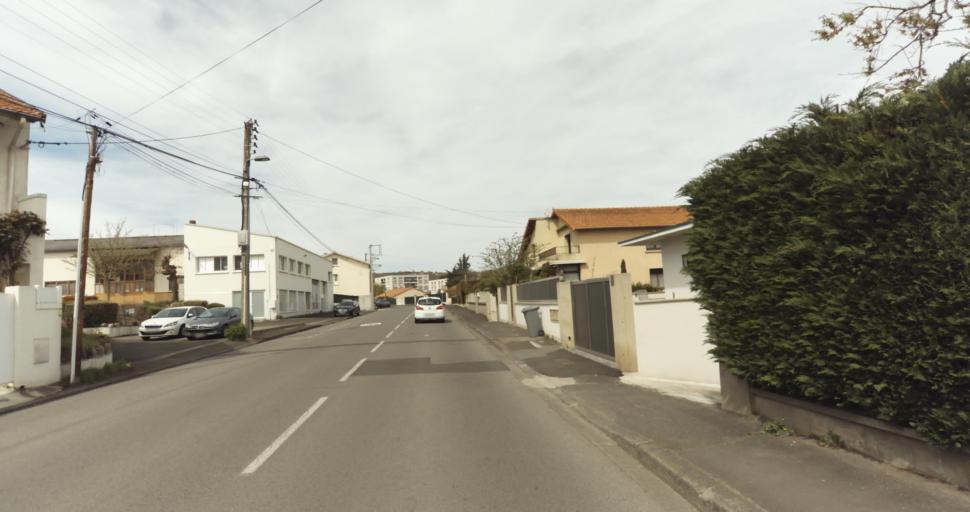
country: FR
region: Auvergne
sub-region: Departement du Puy-de-Dome
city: Cebazat
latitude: 45.8282
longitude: 3.1000
